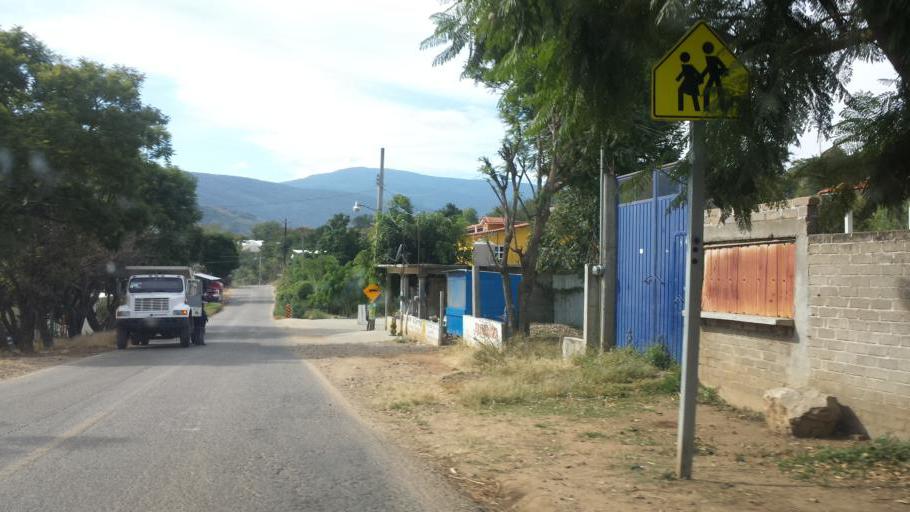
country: MX
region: Oaxaca
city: La Pe
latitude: 16.6151
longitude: -96.8559
